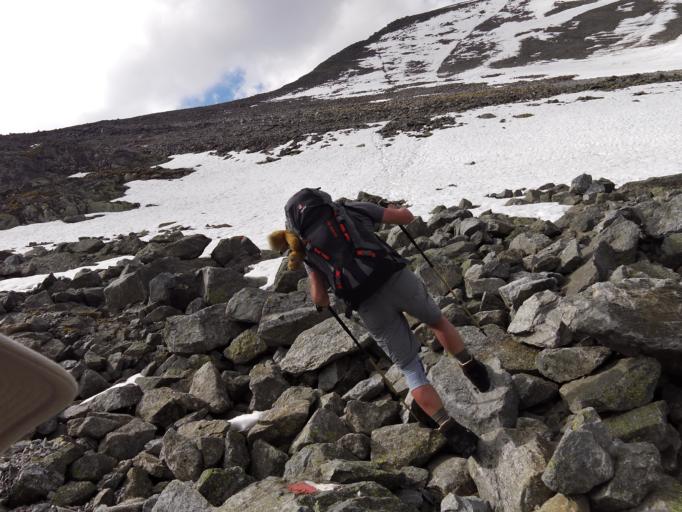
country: AT
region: Tyrol
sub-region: Politischer Bezirk Innsbruck Land
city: Neustift im Stubaital
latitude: 47.0745
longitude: 11.2085
